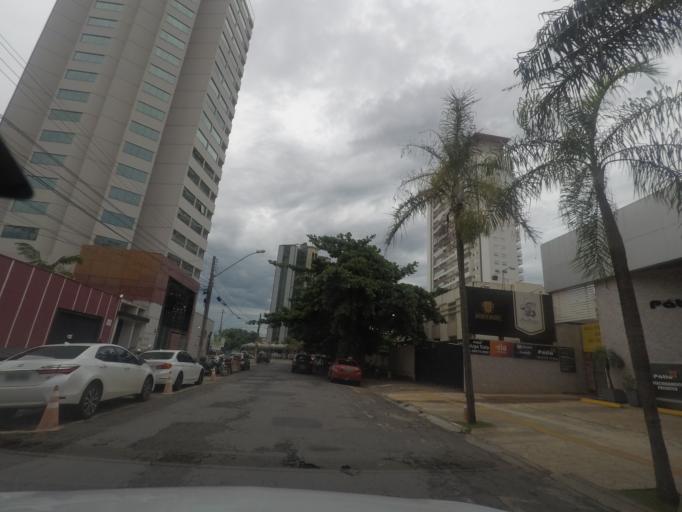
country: BR
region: Goias
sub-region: Goiania
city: Goiania
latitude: -16.6902
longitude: -49.2649
